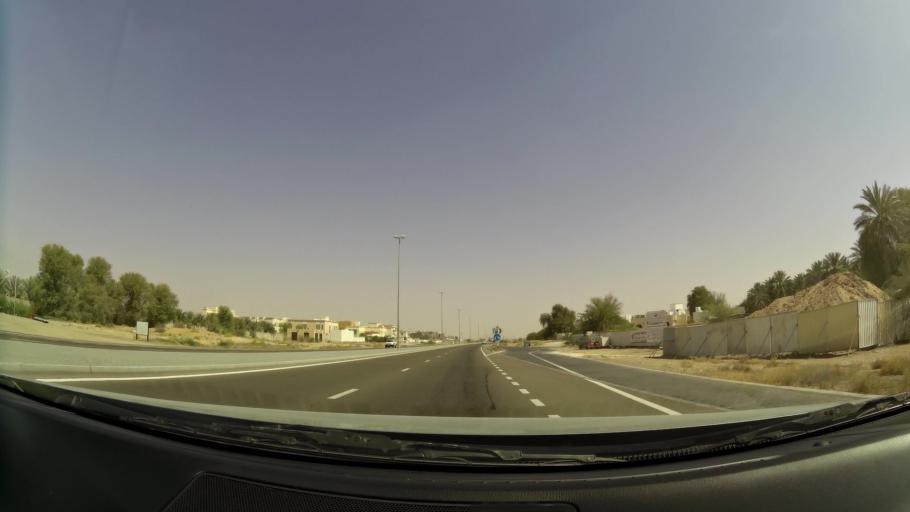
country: OM
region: Al Buraimi
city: Al Buraymi
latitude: 24.2993
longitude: 55.7658
